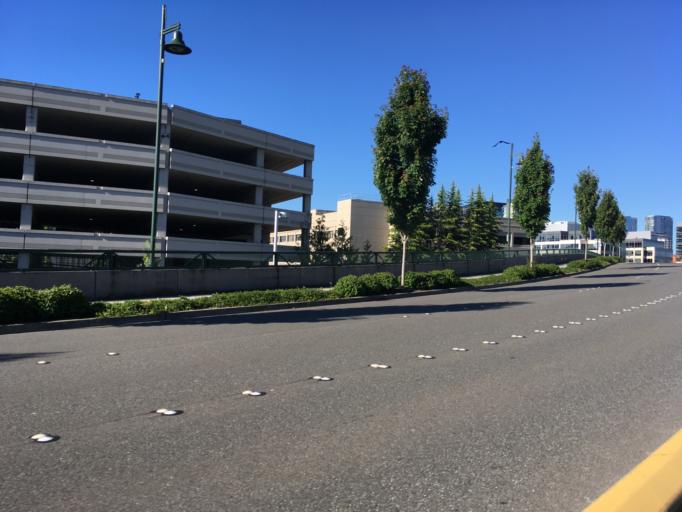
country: US
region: Washington
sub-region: King County
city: Bellevue
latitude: 47.6227
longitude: -122.1868
